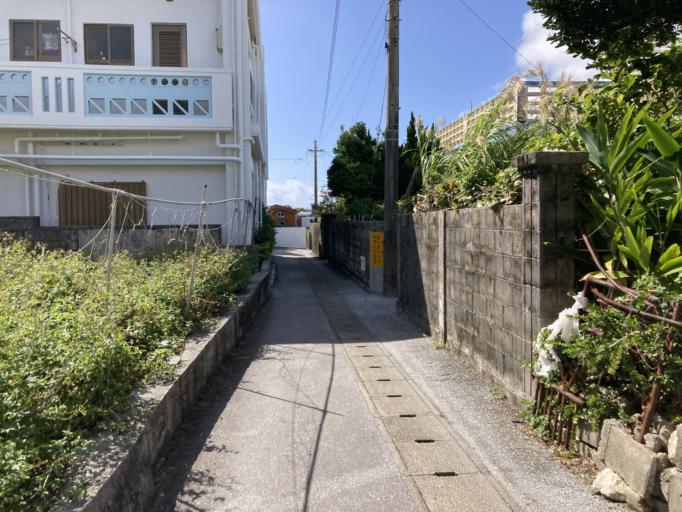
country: JP
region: Okinawa
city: Itoman
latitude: 26.1286
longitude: 127.7718
